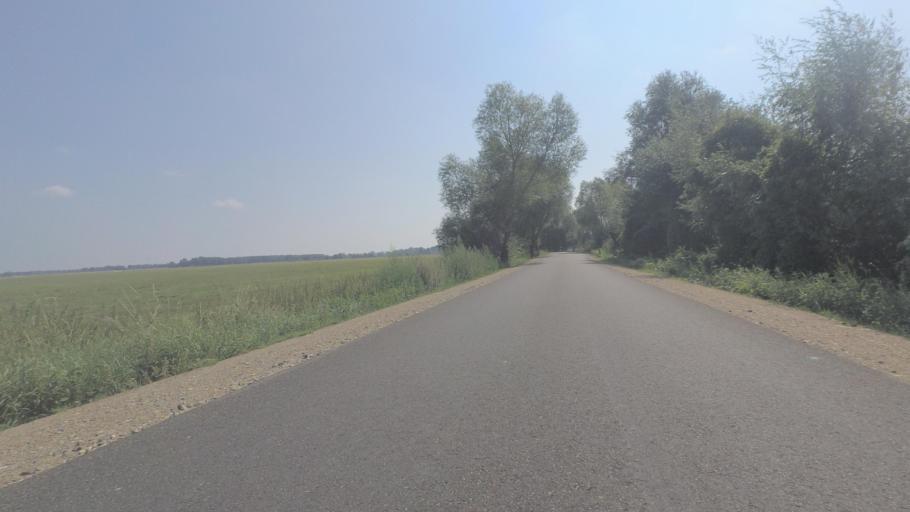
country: DE
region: Mecklenburg-Vorpommern
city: Pampow
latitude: 53.7280
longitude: 12.6710
